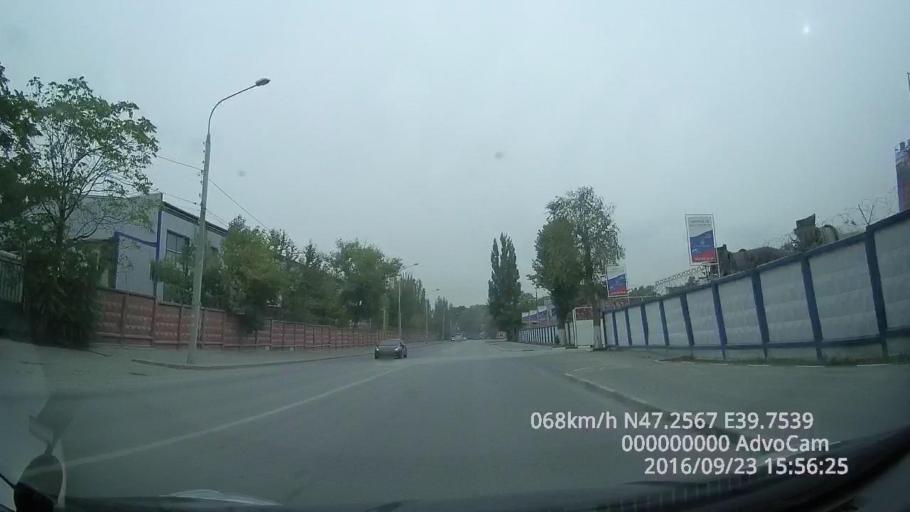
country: RU
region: Rostov
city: Imeni Chkalova
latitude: 47.2567
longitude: 39.7540
